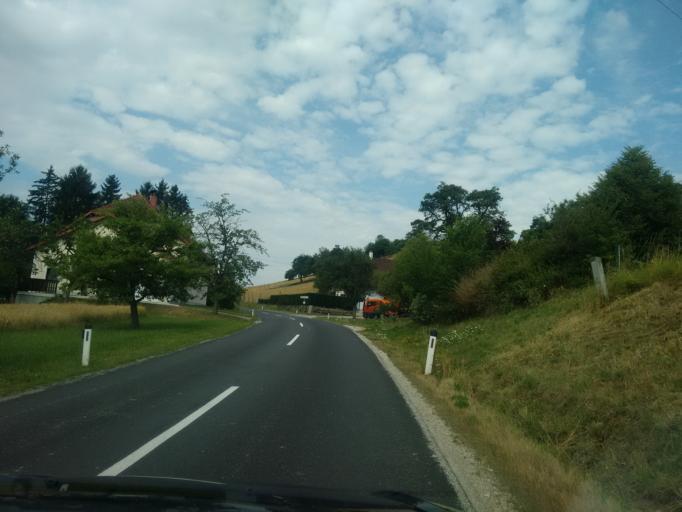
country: AT
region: Upper Austria
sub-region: Politischer Bezirk Grieskirchen
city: Grieskirchen
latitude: 48.2004
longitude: 13.8651
